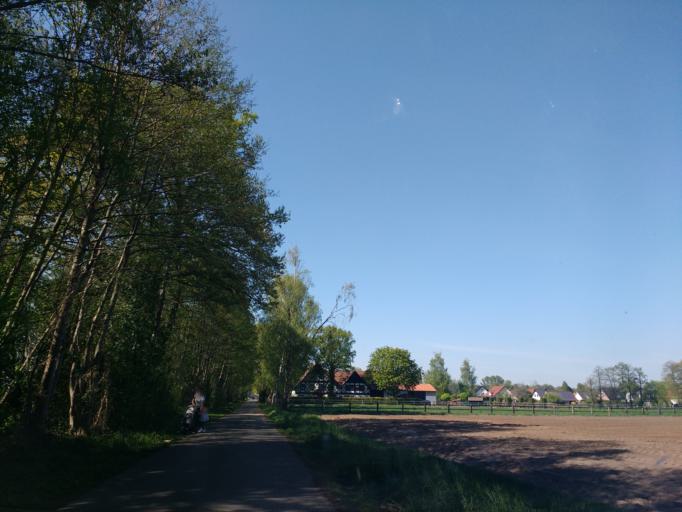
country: DE
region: North Rhine-Westphalia
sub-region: Regierungsbezirk Detmold
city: Delbruck
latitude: 51.7530
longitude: 8.5706
